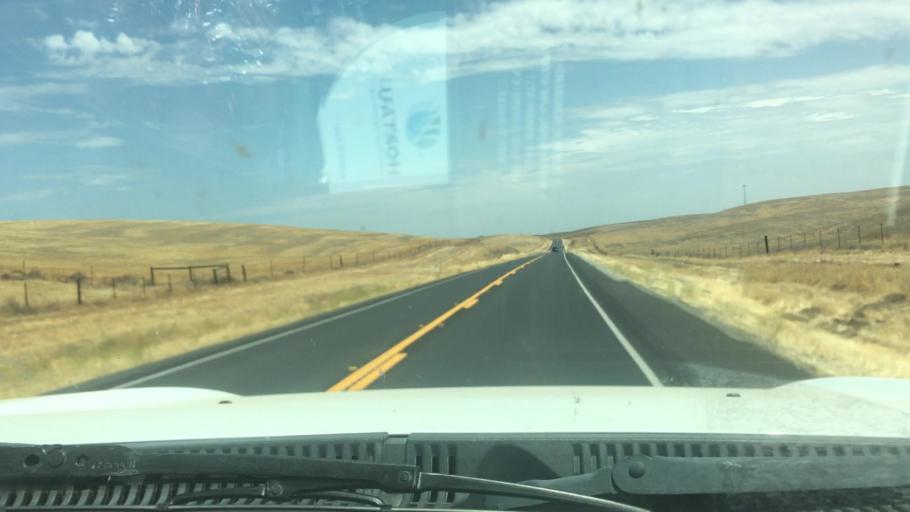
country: US
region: California
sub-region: Kern County
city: McFarland
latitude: 35.6129
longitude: -119.0869
